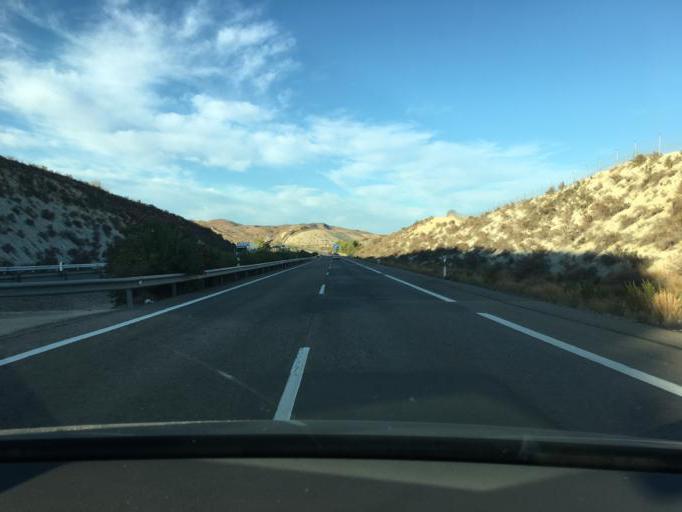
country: ES
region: Andalusia
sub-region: Provincia de Almeria
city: Bedar
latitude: 37.1201
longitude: -2.0184
